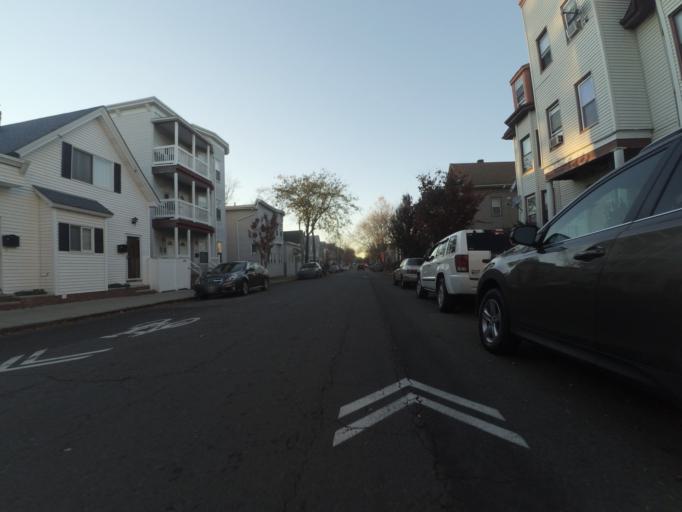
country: US
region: Massachusetts
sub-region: Middlesex County
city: Somerville
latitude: 42.3859
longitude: -71.0885
